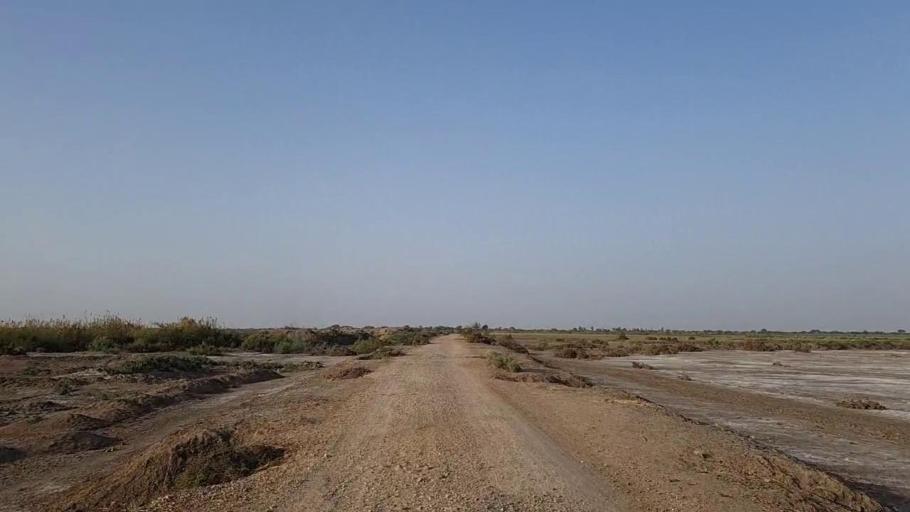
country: PK
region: Sindh
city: Jati
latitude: 24.3716
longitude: 68.1469
